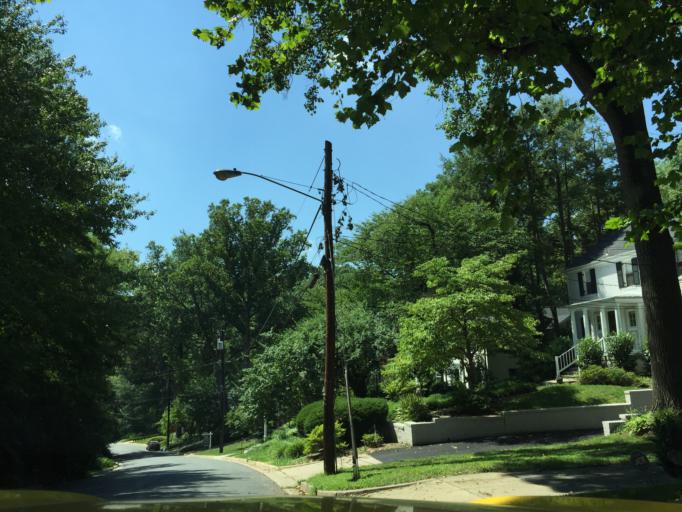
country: US
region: Maryland
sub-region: Montgomery County
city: Somerset
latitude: 38.9493
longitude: -77.1026
